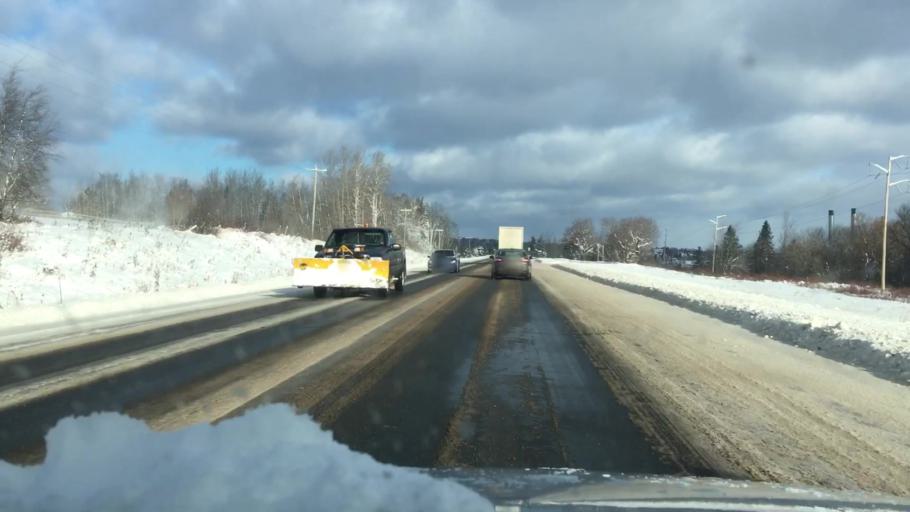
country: US
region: Maine
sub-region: Aroostook County
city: Caribou
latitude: 46.8440
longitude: -68.0034
